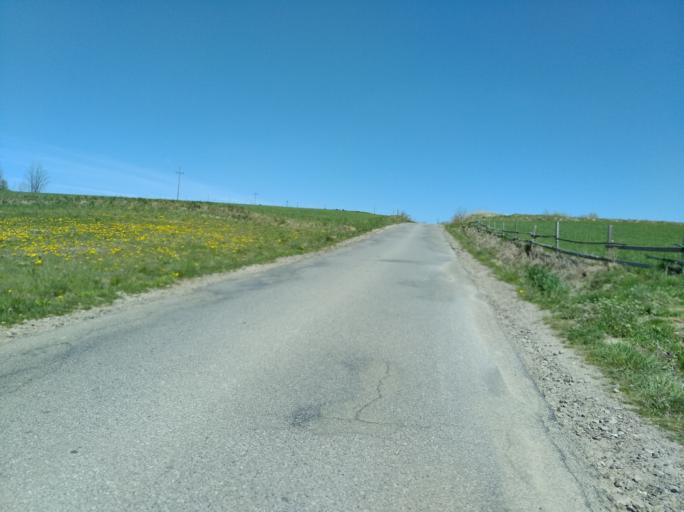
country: PL
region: Subcarpathian Voivodeship
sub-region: Powiat brzozowski
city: Jablonka
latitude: 49.7261
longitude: 22.1133
